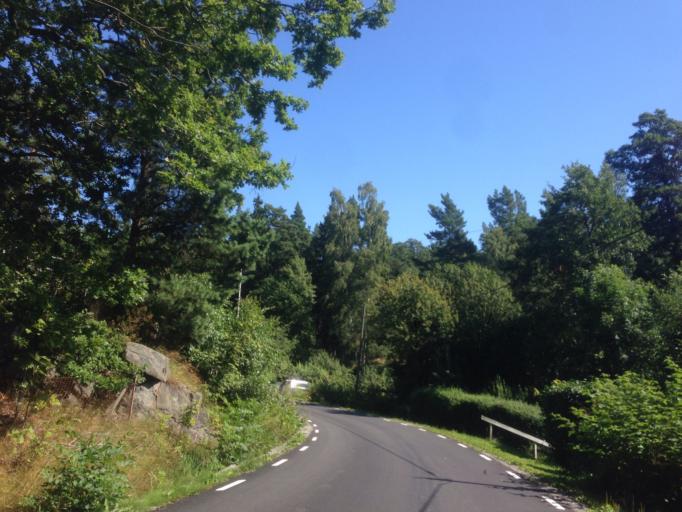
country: SE
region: Stockholm
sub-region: Vaxholms Kommun
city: Vaxholm
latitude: 59.3858
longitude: 18.3673
